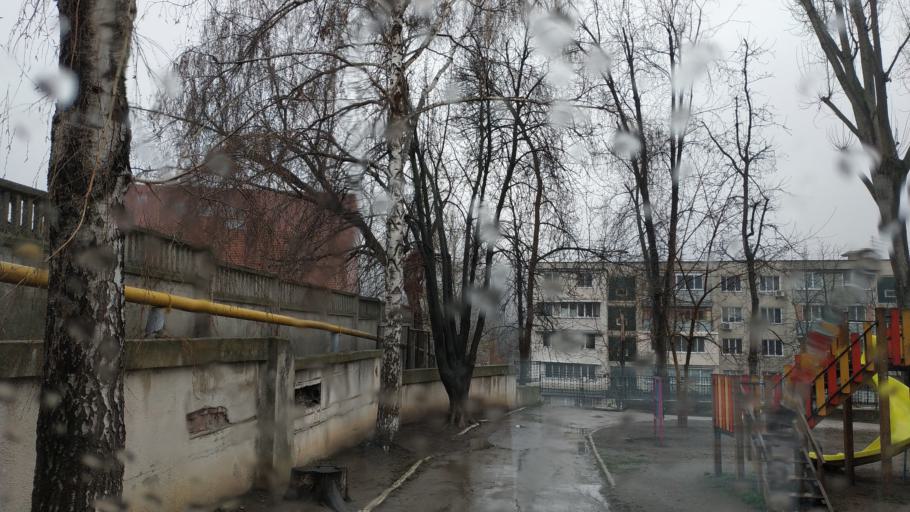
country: MD
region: Chisinau
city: Chisinau
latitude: 47.0196
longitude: 28.7997
